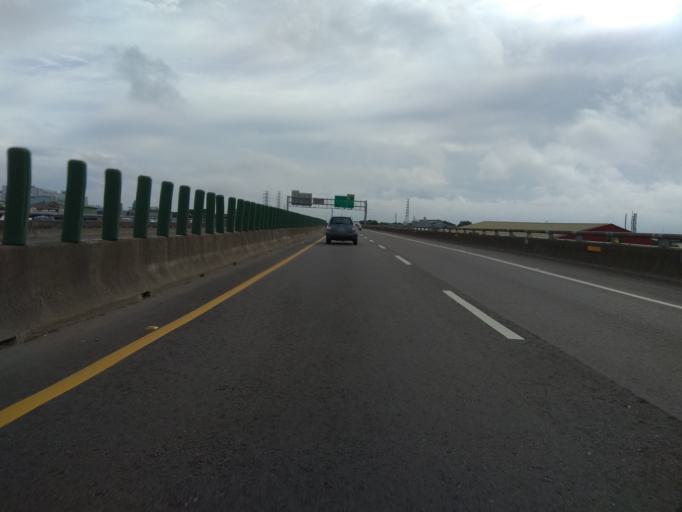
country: TW
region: Taiwan
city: Daxi
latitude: 24.8994
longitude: 121.2439
